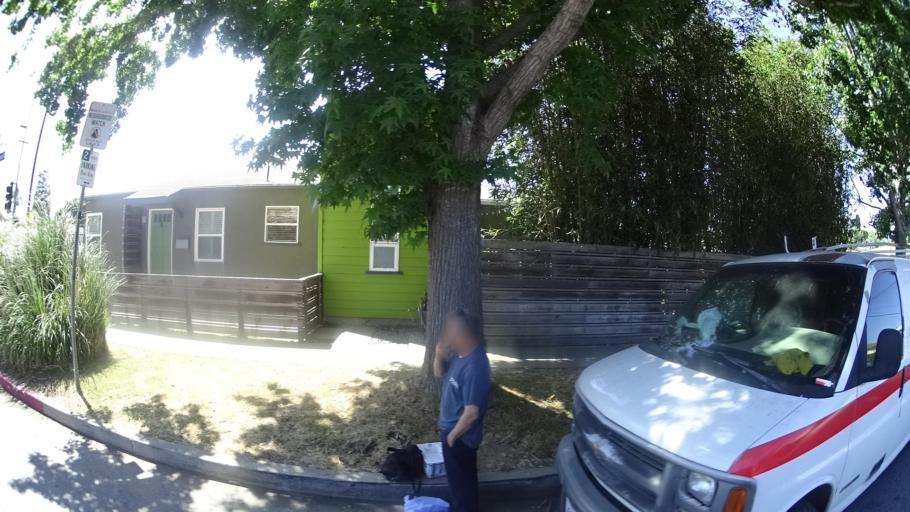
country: US
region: California
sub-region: Los Angeles County
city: Westwood, Los Angeles
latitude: 34.0269
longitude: -118.4486
